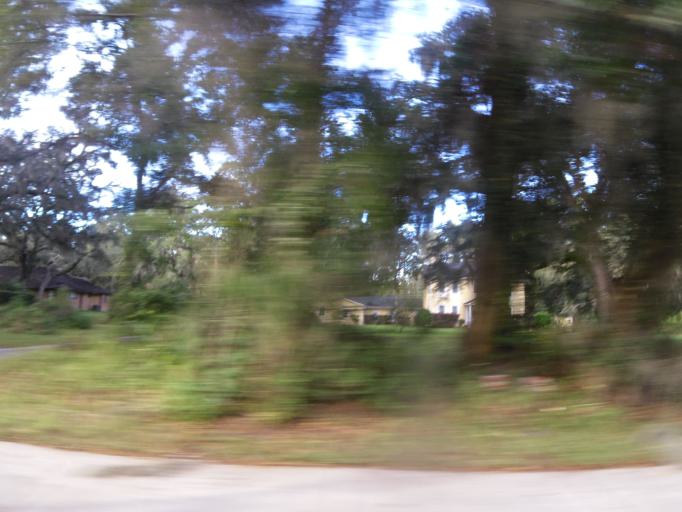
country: US
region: Florida
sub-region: Saint Johns County
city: Fruit Cove
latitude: 30.1593
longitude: -81.6092
